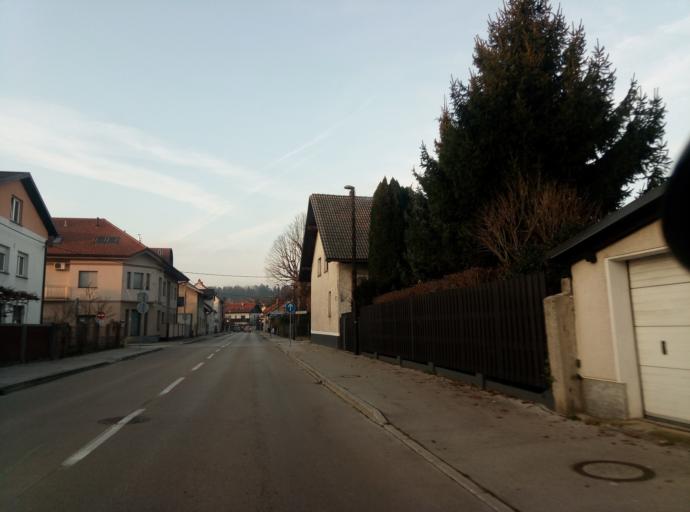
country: SI
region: Ljubljana
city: Ljubljana
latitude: 46.0474
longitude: 14.4859
